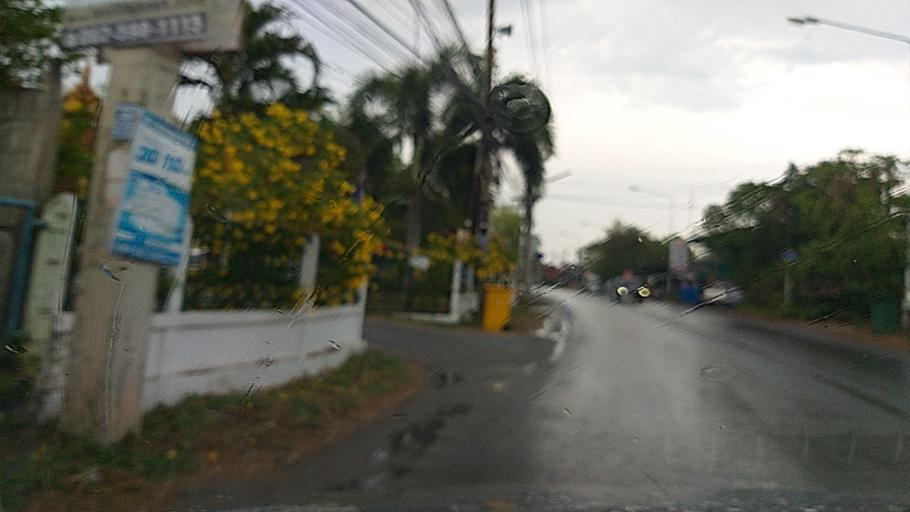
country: TH
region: Phra Nakhon Si Ayutthaya
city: Phra Nakhon Si Ayutthaya
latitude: 14.3401
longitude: 100.5409
